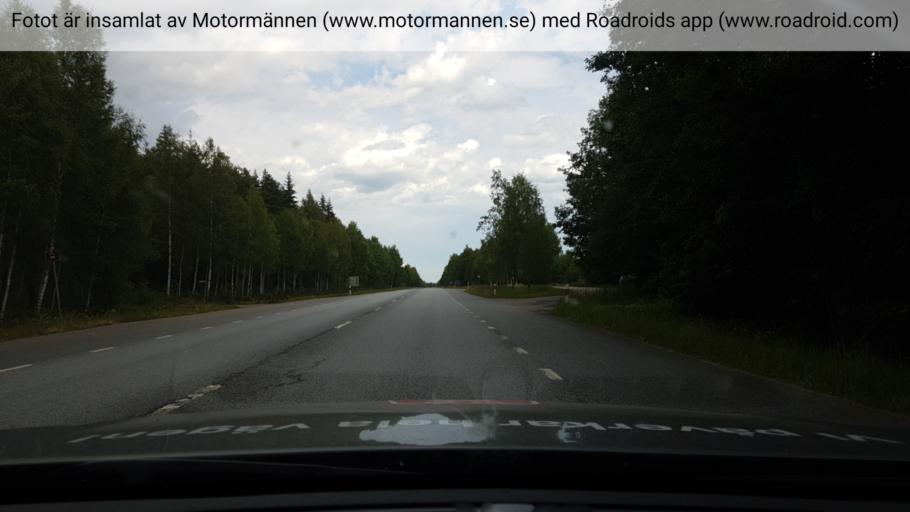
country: SE
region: Uppsala
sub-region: Heby Kommun
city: Morgongava
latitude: 59.8958
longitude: 17.1199
